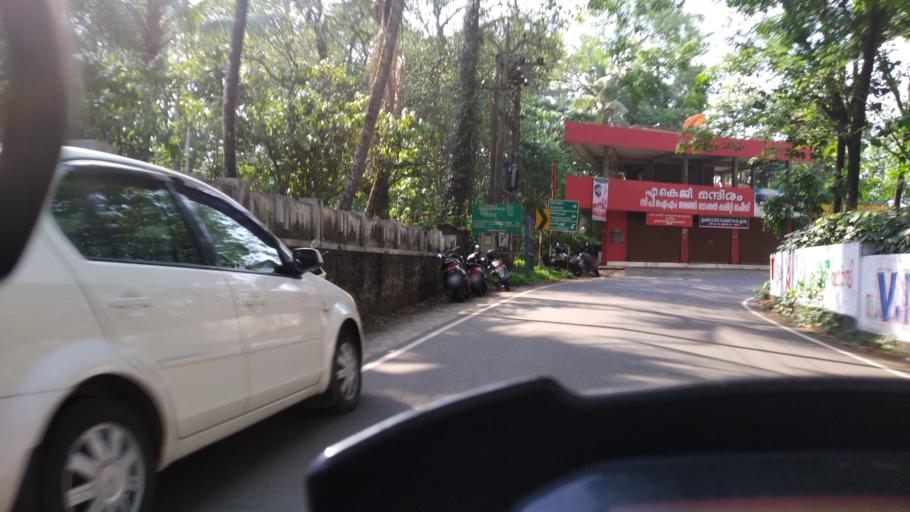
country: IN
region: Kerala
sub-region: Ernakulam
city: Piravam
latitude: 9.8316
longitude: 76.5450
